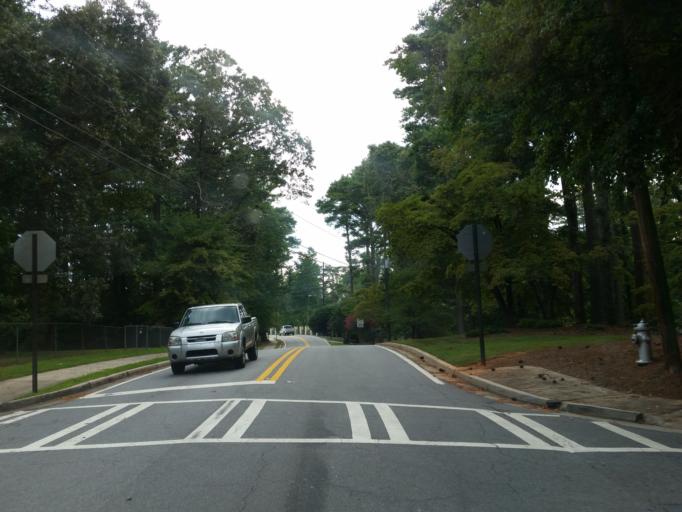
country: US
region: Georgia
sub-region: Fulton County
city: Sandy Springs
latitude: 33.9509
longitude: -84.4253
